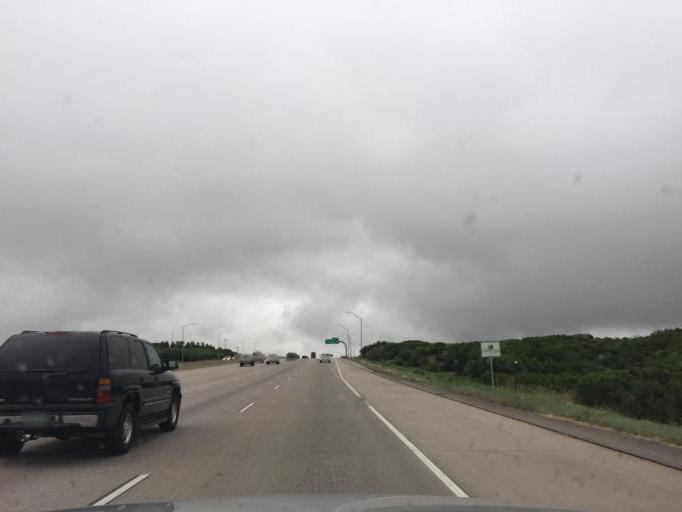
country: US
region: Colorado
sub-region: Park County
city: Castle Pines North
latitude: 39.4648
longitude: -104.8736
